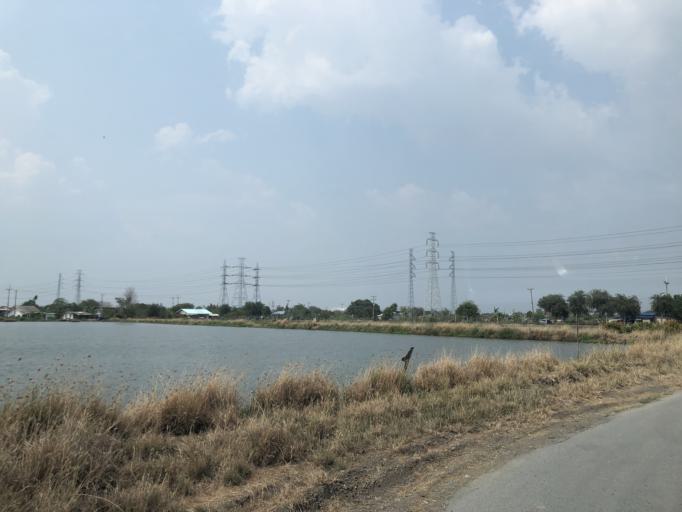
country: TH
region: Samut Prakan
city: Bang Bo
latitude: 13.5433
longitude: 100.8805
